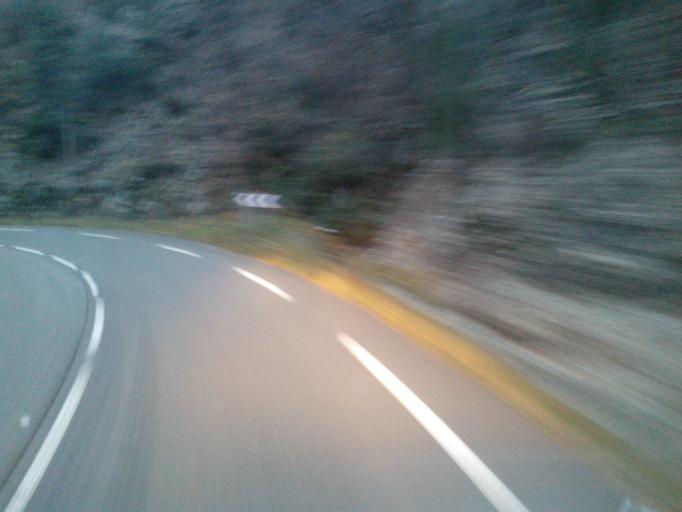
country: FR
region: Languedoc-Roussillon
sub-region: Departement du Gard
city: Saint-Jean-du-Gard
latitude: 44.1376
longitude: 3.7824
